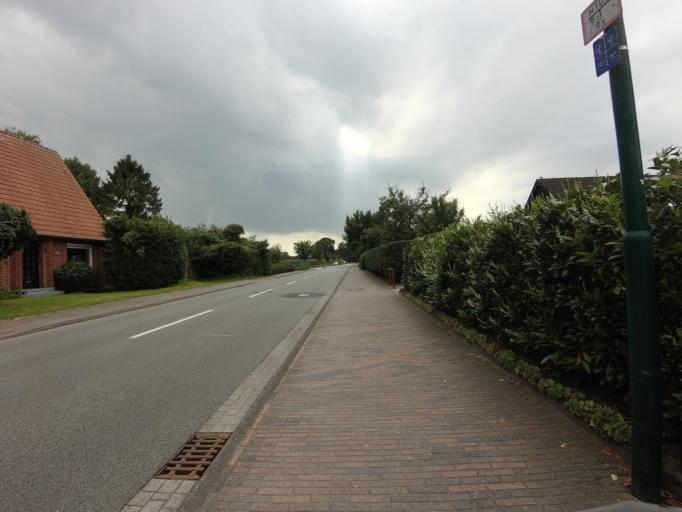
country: DE
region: Lower Saxony
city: Lage
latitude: 52.4646
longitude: 6.9588
